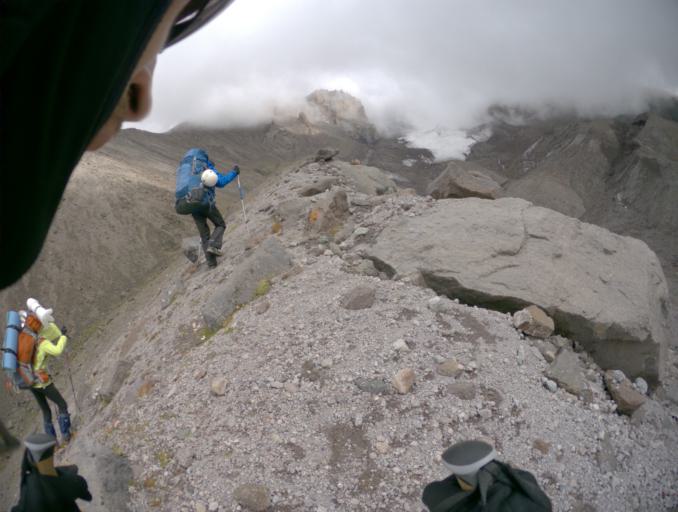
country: RU
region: Kabardino-Balkariya
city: Terskol
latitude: 43.3819
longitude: 42.3841
